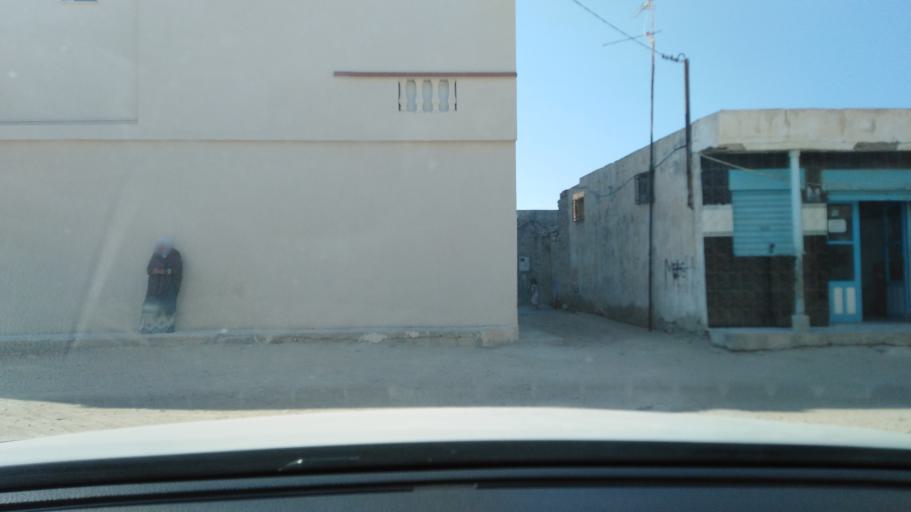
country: TN
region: Qabis
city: Gabes
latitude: 33.9404
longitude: 10.0690
